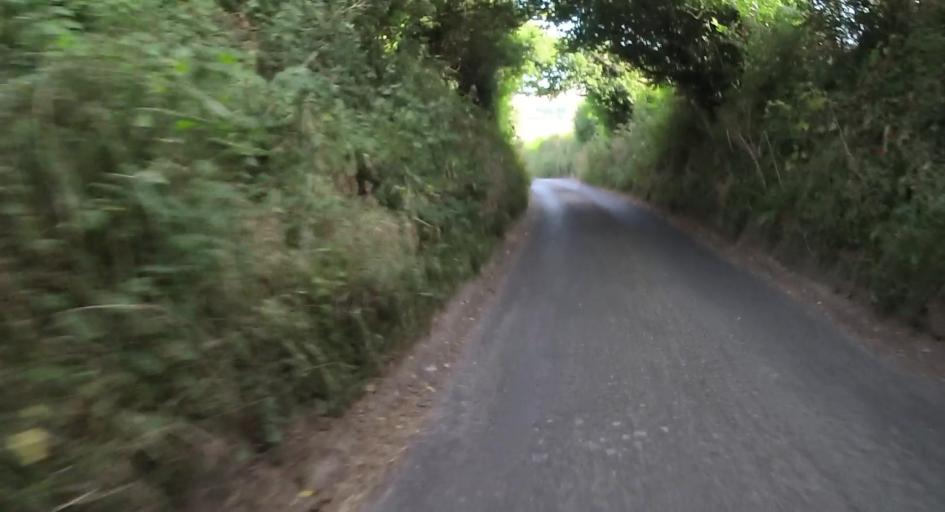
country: GB
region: England
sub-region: Dorset
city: Wareham
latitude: 50.6362
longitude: -2.0952
